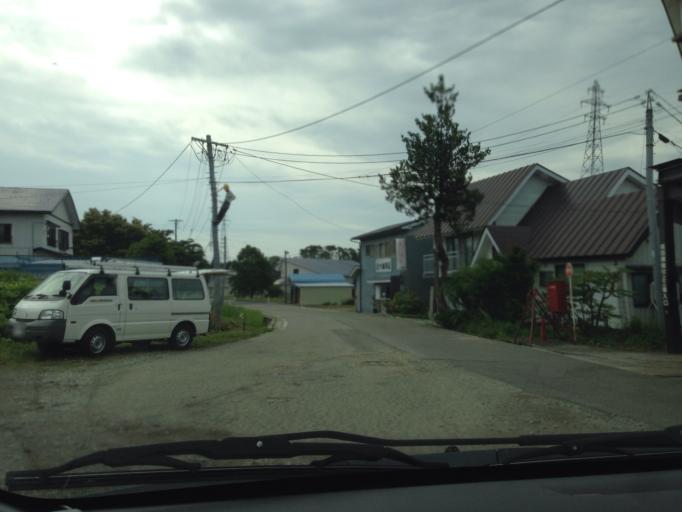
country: JP
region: Fukushima
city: Inawashiro
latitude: 37.5521
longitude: 140.0545
